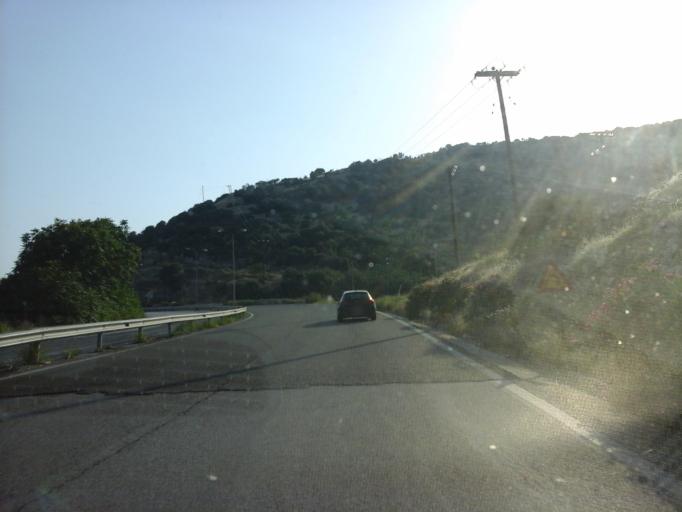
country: GR
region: East Macedonia and Thrace
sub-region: Nomos Kavalas
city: Kavala
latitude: 40.9555
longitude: 24.4579
